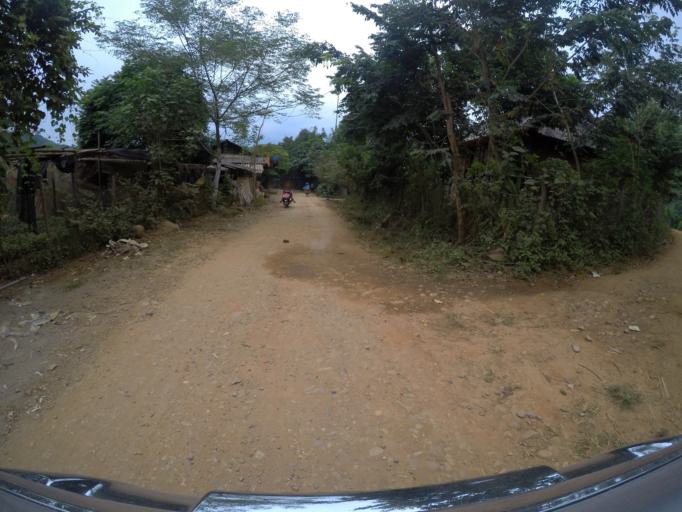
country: VN
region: Yen Bai
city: Son Thinh
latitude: 21.6815
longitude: 104.6082
